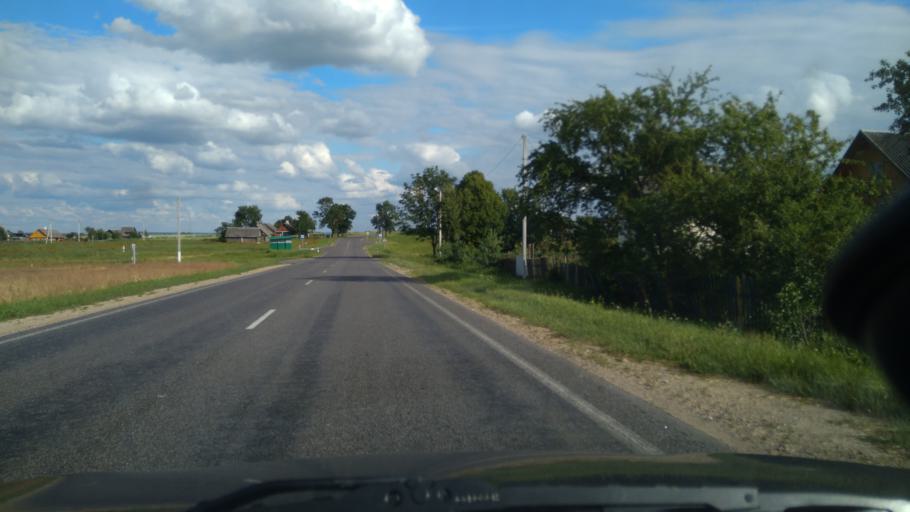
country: BY
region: Grodnenskaya
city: Masty
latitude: 53.3139
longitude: 24.6934
